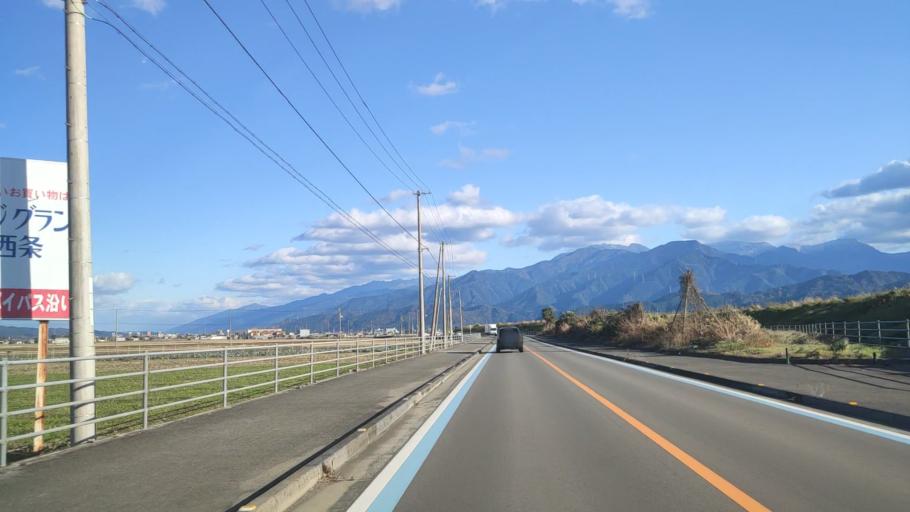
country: JP
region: Ehime
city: Saijo
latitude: 33.9100
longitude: 133.1364
